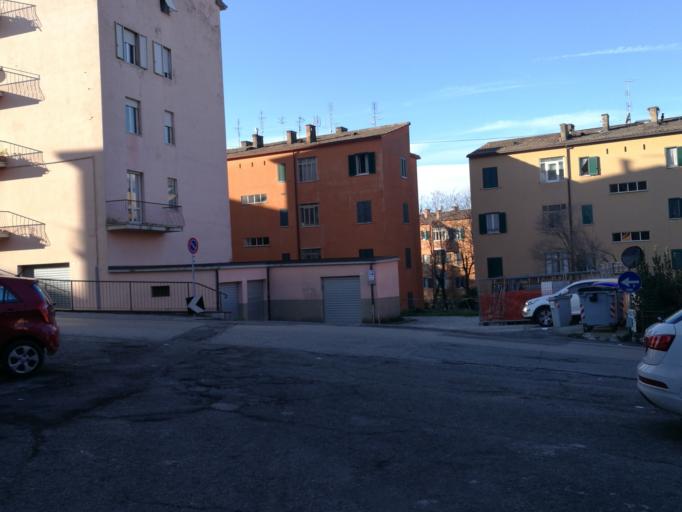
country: IT
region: Umbria
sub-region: Provincia di Perugia
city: Perugia
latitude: 43.0973
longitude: 12.3906
